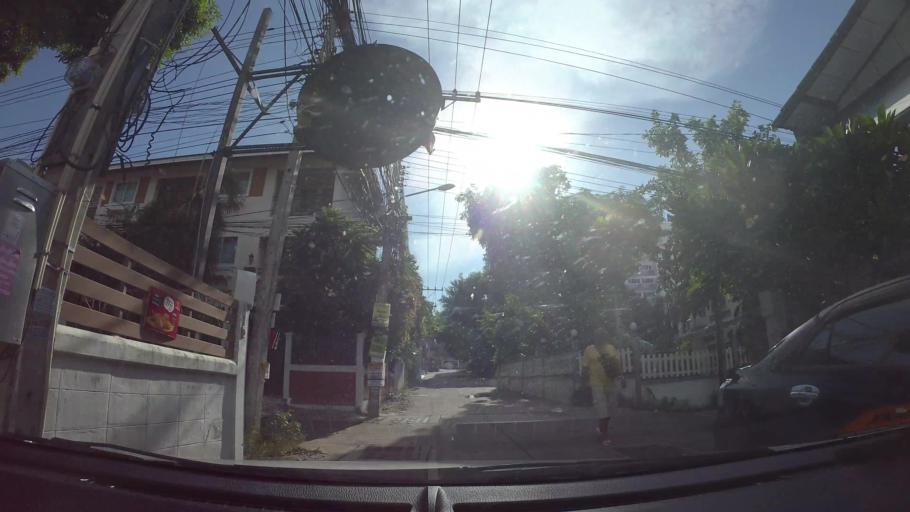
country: TH
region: Chon Buri
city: Phatthaya
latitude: 12.9151
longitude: 100.8721
